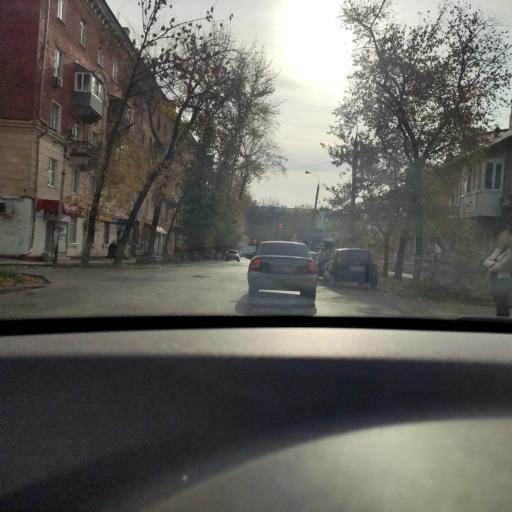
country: RU
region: Samara
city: Petra-Dubrava
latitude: 53.2270
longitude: 50.2768
